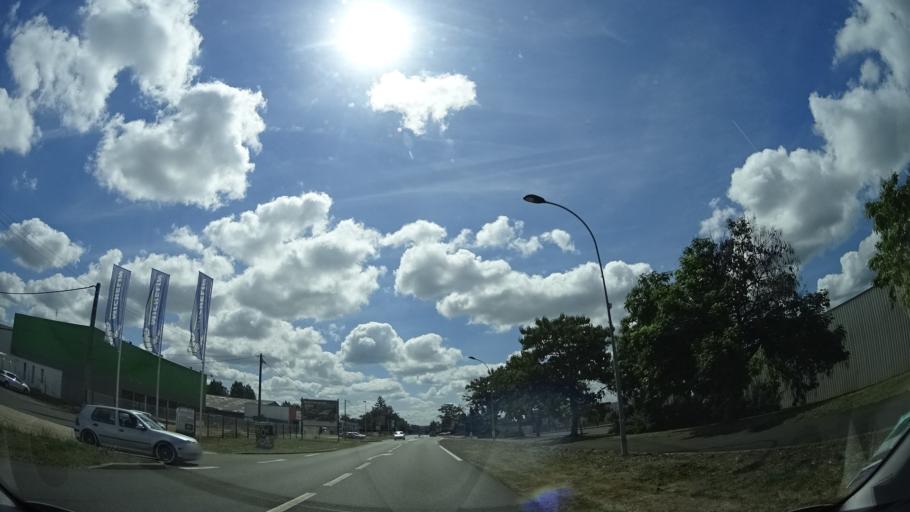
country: FR
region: Pays de la Loire
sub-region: Departement de la Sarthe
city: La Fleche
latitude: 47.7086
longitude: -0.0967
